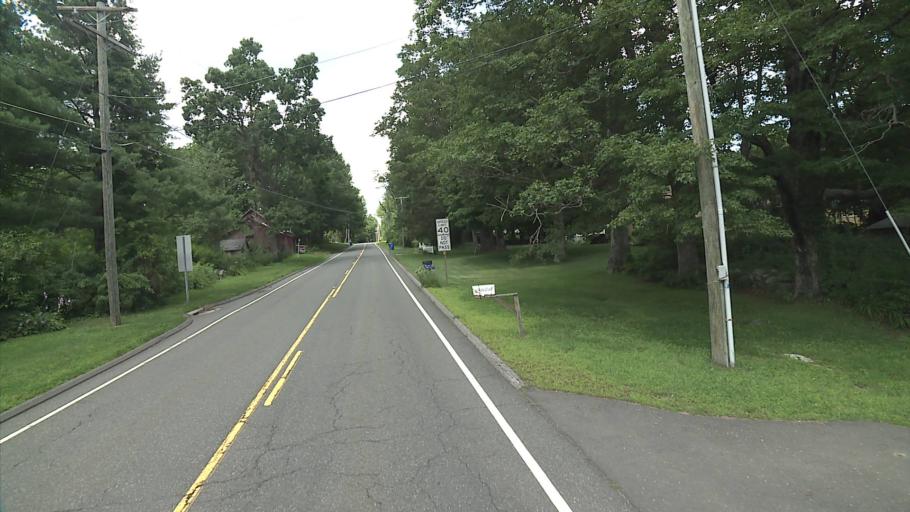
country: US
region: Massachusetts
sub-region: Hampden County
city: Granville
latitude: 42.0100
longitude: -72.9707
